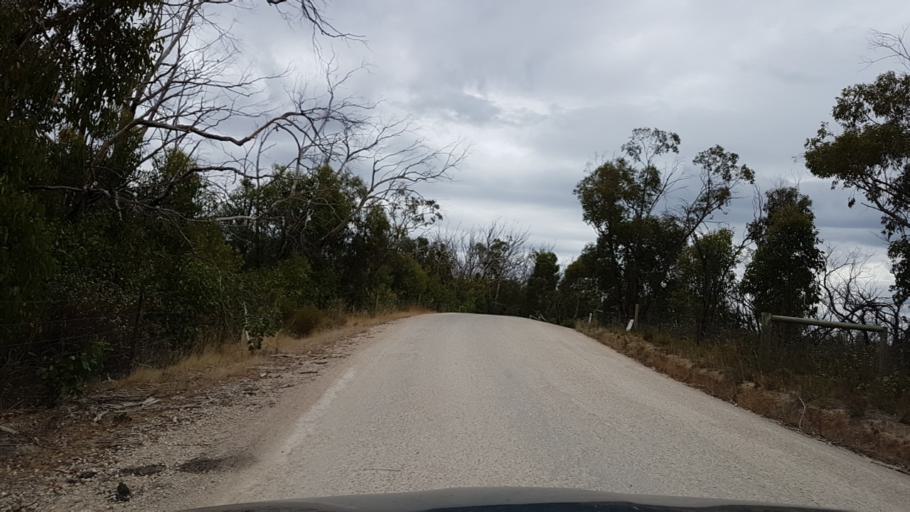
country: AU
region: South Australia
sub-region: Tea Tree Gully
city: Golden Grove
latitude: -34.7748
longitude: 138.8145
